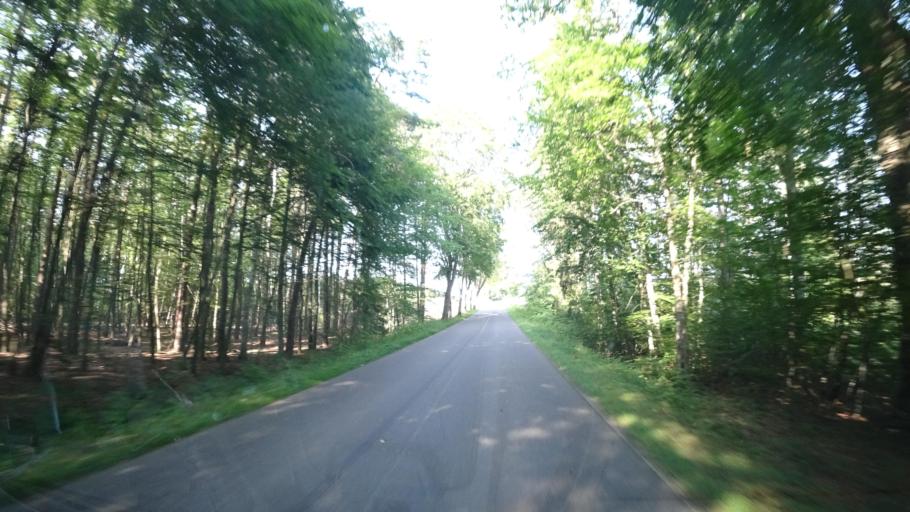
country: PL
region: Pomeranian Voivodeship
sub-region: Powiat czluchowski
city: Rzeczenica
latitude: 53.7892
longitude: 17.1737
